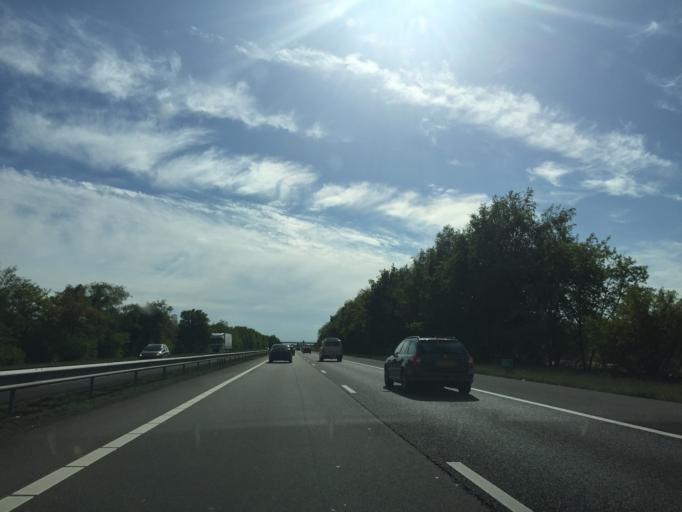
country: NL
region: Gelderland
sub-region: Gemeente Barneveld
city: Kootwijkerbroek
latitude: 52.1757
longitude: 5.6450
